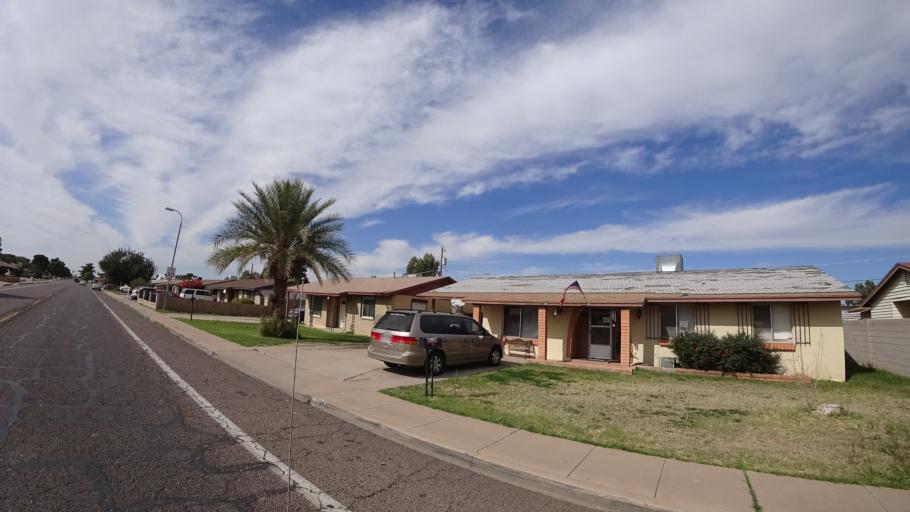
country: US
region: Arizona
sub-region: Maricopa County
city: Glendale
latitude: 33.4733
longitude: -112.1487
